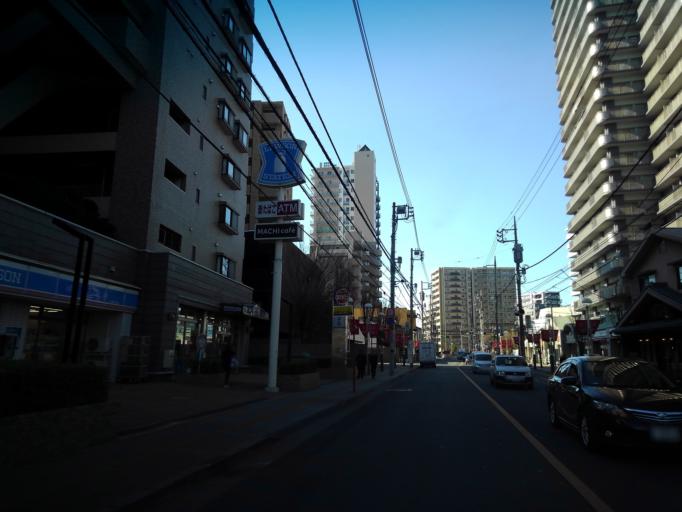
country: JP
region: Saitama
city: Tokorozawa
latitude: 35.7914
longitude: 139.4662
